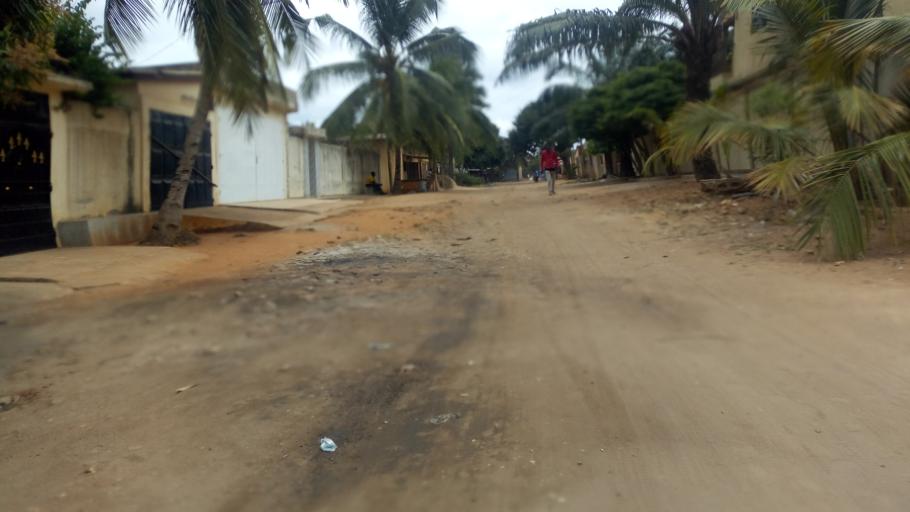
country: TG
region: Maritime
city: Lome
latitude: 6.2331
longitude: 1.1836
